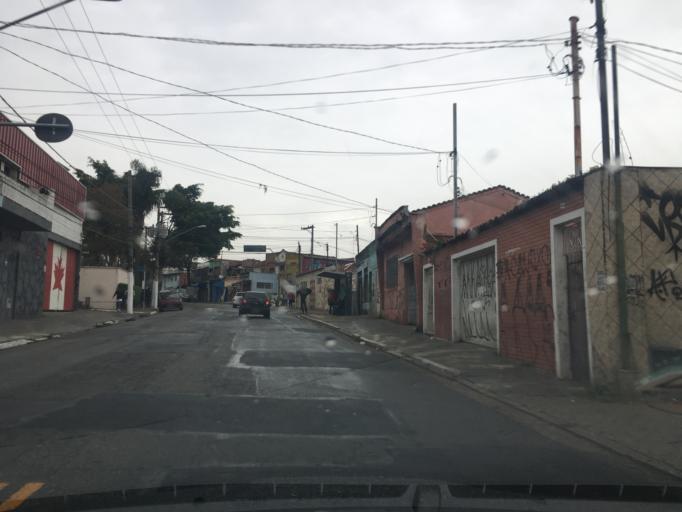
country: BR
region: Sao Paulo
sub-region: Guarulhos
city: Guarulhos
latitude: -23.5172
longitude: -46.5497
